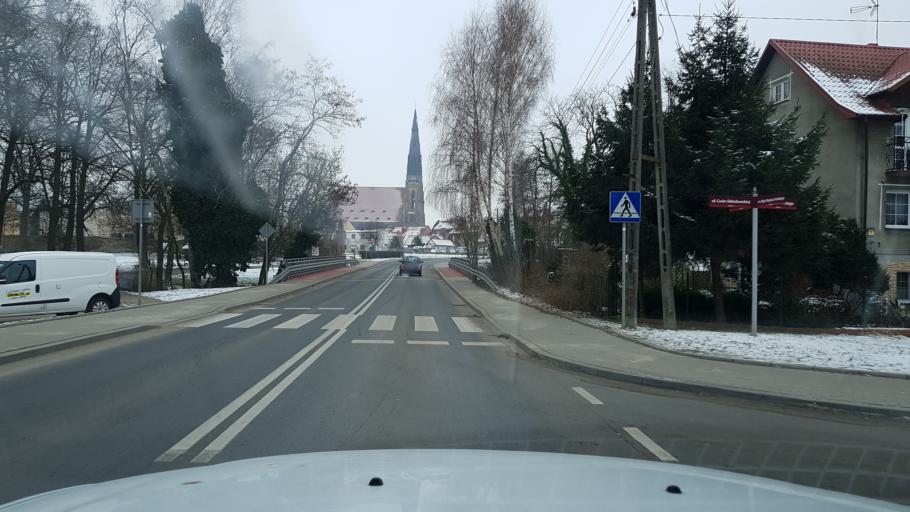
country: PL
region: West Pomeranian Voivodeship
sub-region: Powiat gryfinski
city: Chojna
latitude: 52.9668
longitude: 14.4289
